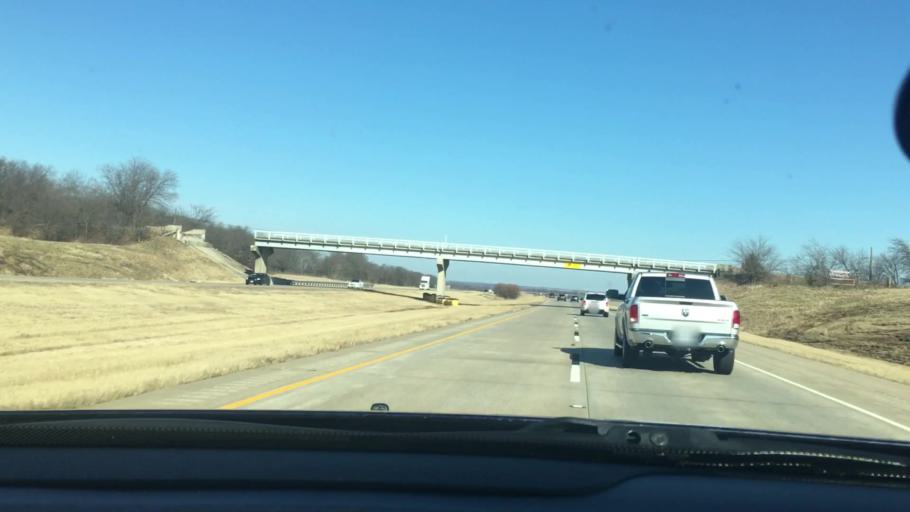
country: US
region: Oklahoma
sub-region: Love County
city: Marietta
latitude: 33.9611
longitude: -97.1340
